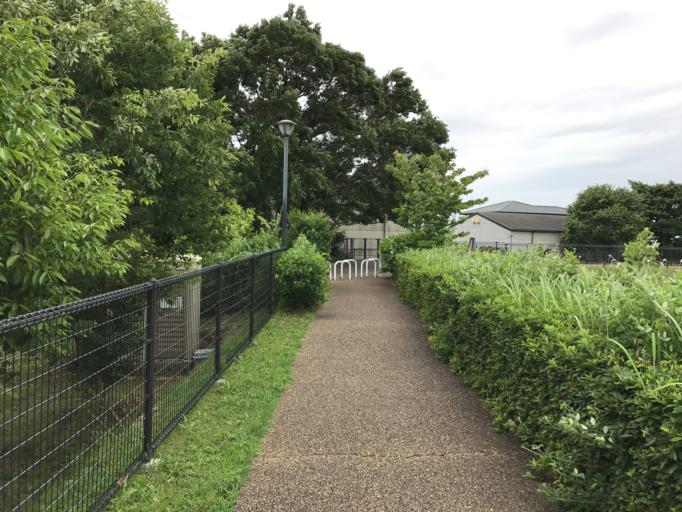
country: JP
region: Osaka
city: Yao
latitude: 34.6382
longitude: 135.6405
